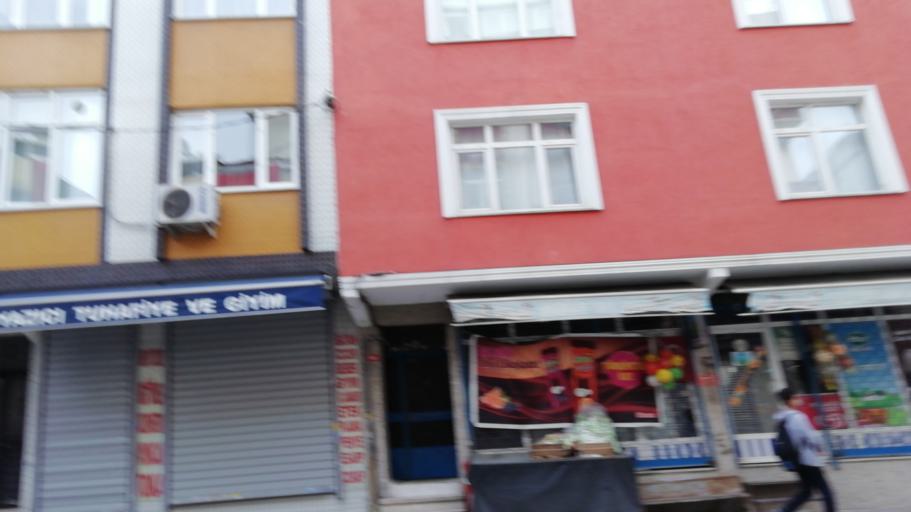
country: TR
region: Istanbul
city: Bagcilar
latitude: 41.0290
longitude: 28.8397
